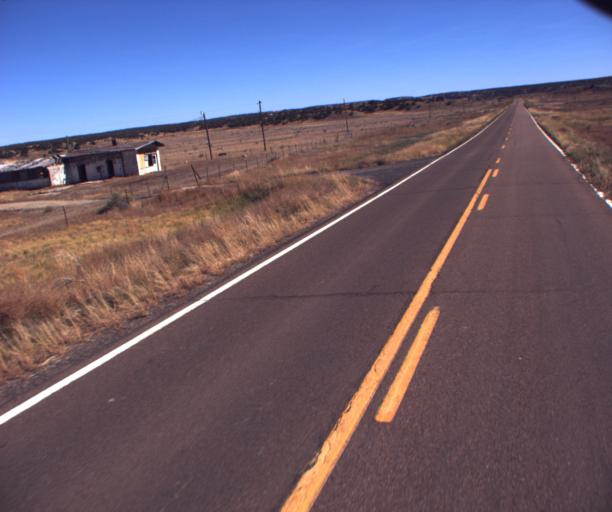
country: US
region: Arizona
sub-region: Apache County
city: Ganado
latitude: 35.7506
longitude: -109.8815
